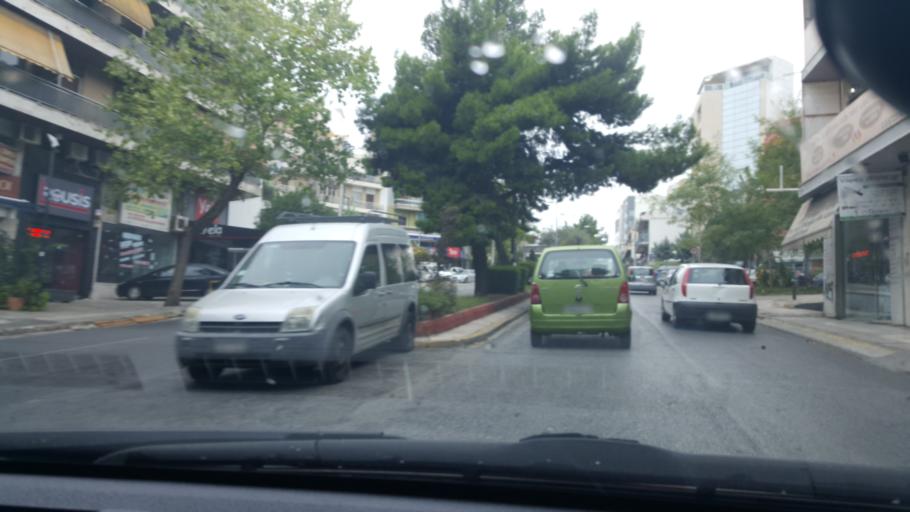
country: GR
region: Attica
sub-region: Nomarchia Athinas
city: Neo Psychiko
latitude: 37.9946
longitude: 23.7740
